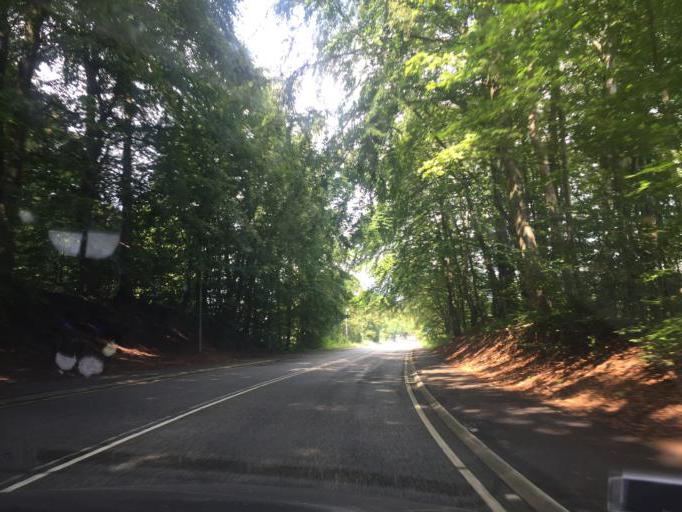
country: DK
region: Capital Region
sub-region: Rudersdal Kommune
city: Holte
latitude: 55.7777
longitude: 12.4486
